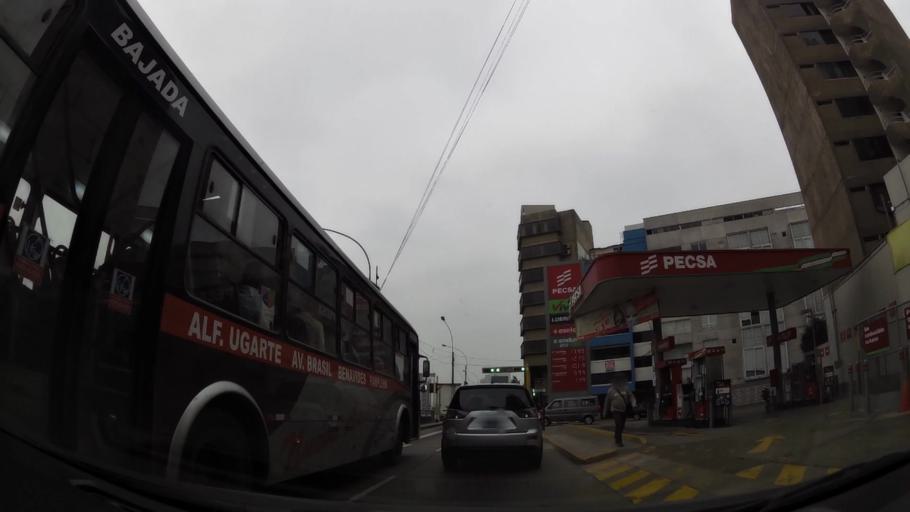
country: PE
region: Lima
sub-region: Lima
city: Surco
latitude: -12.1233
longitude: -77.0249
